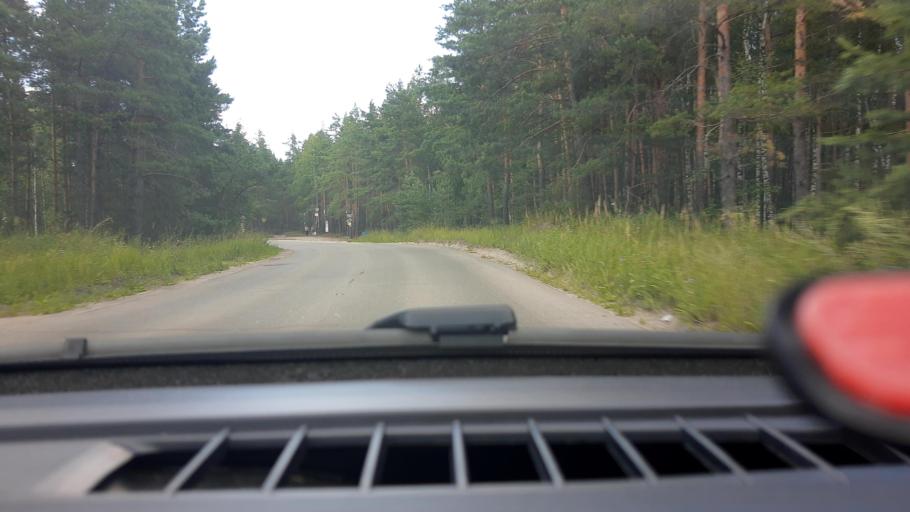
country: RU
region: Nizjnij Novgorod
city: Babino
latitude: 56.3234
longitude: 43.6337
